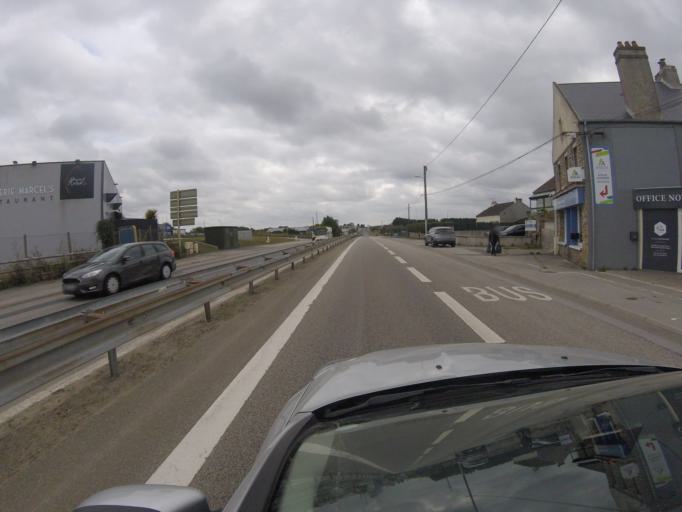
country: FR
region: Lower Normandy
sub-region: Departement de la Manche
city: La Glacerie
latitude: 49.6082
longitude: -1.5998
